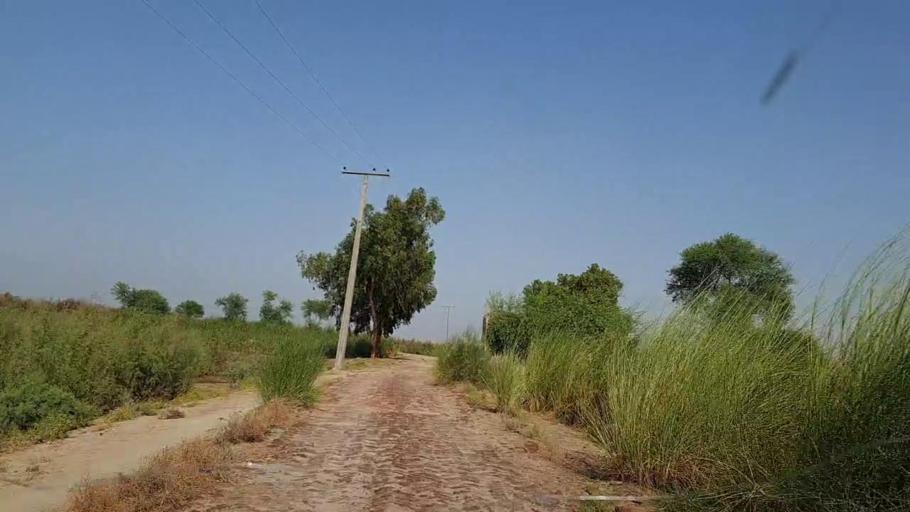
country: PK
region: Sindh
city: Khanpur
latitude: 27.6756
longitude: 69.3747
